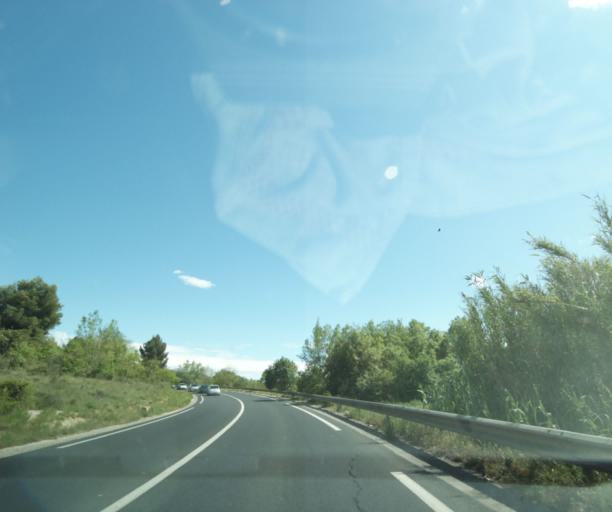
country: FR
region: Languedoc-Roussillon
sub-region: Departement de l'Herault
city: Saint-Jean-de-Vedas
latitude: 43.5904
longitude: 3.8208
